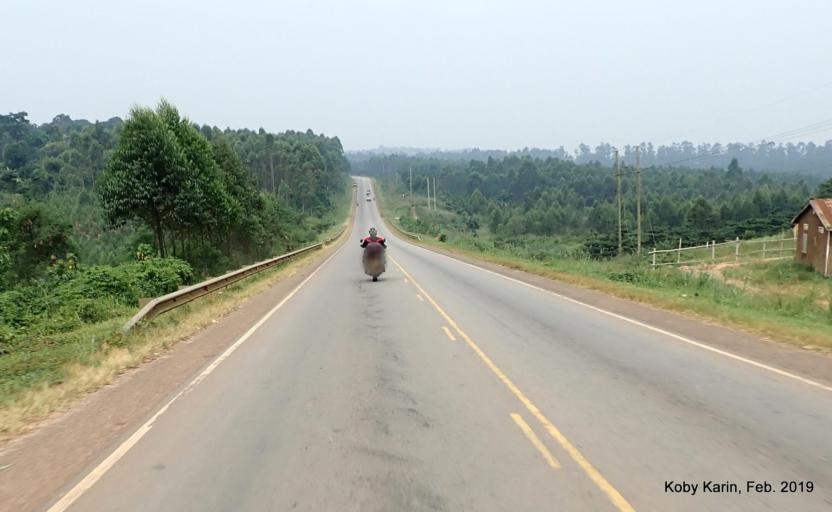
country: UG
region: Central Region
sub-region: Wakiso District
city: Wakiso
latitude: 0.3303
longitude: 32.4096
